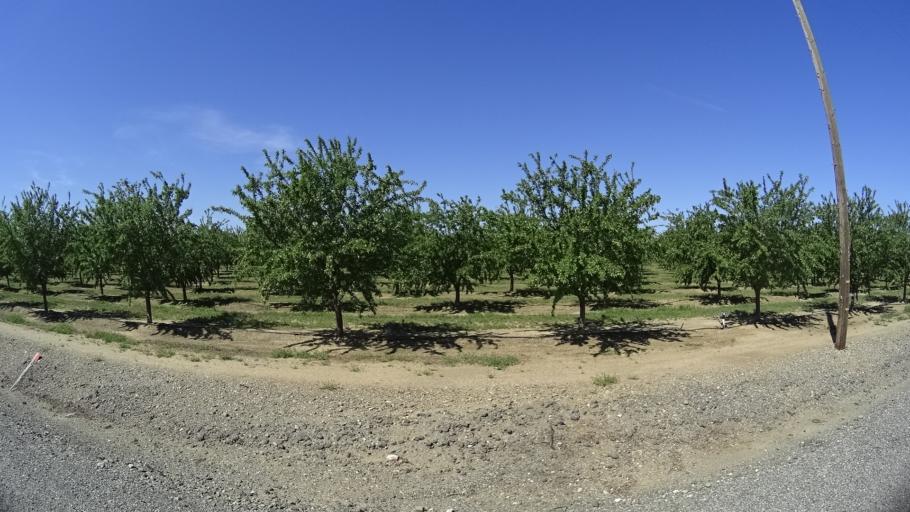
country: US
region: California
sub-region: Glenn County
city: Orland
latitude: 39.6805
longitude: -122.1404
